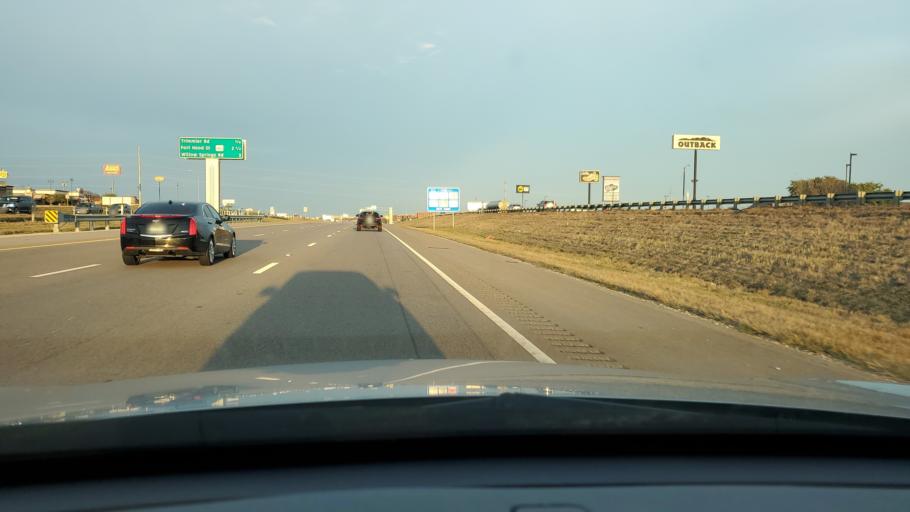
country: US
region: Texas
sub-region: Bell County
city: Killeen
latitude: 31.0861
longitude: -97.7098
